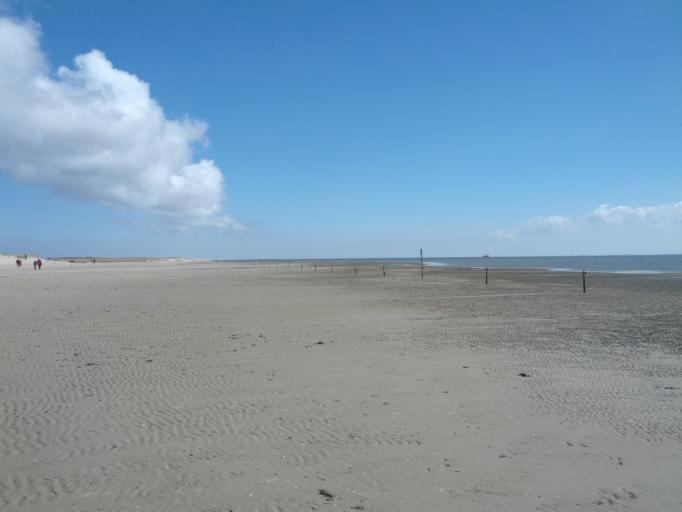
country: DE
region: Lower Saxony
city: Spiekeroog
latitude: 53.7465
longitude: 7.6218
